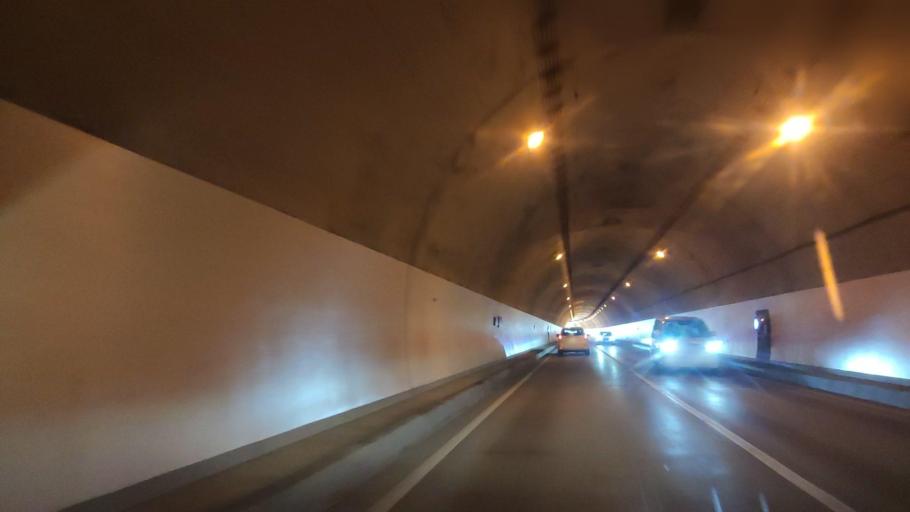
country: JP
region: Hokkaido
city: Ishikari
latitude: 43.4734
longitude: 141.3956
